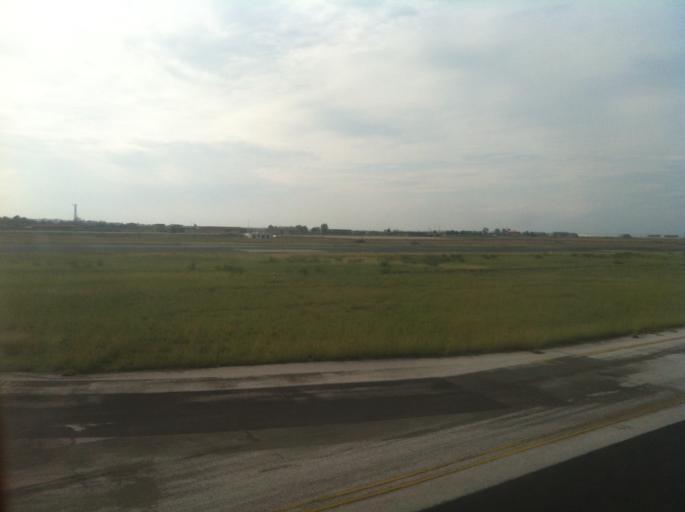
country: GR
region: Central Macedonia
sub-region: Nomos Thessalonikis
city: Neo Rysi
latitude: 40.5102
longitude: 22.9758
